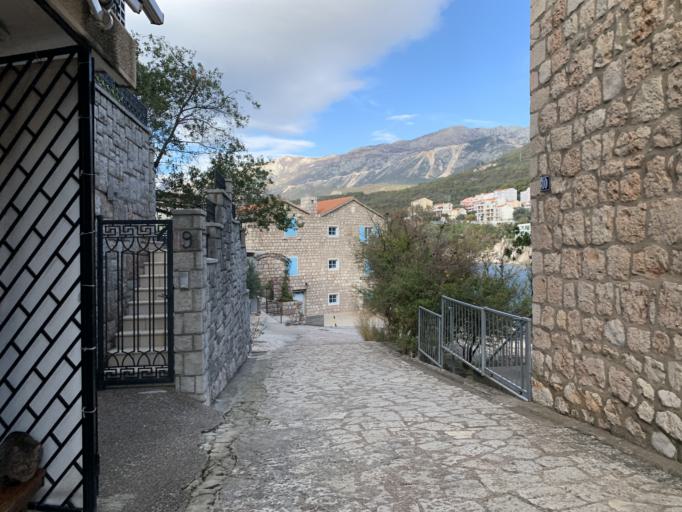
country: ME
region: Budva
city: Budva
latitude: 42.2667
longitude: 18.8915
